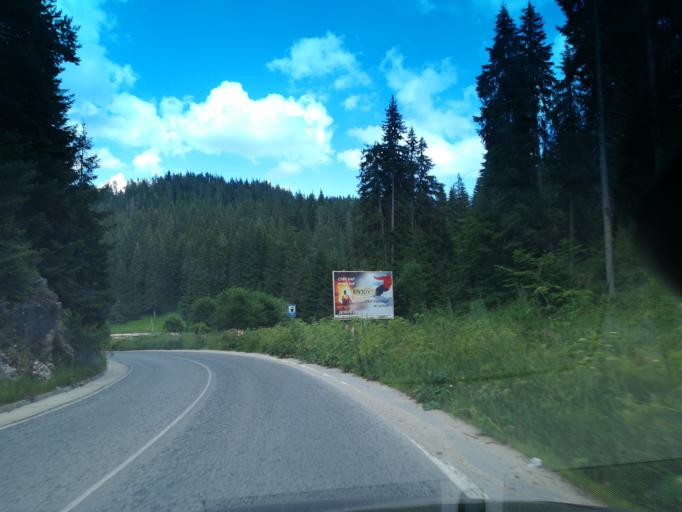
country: BG
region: Smolyan
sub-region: Obshtina Smolyan
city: Smolyan
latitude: 41.6579
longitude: 24.7103
